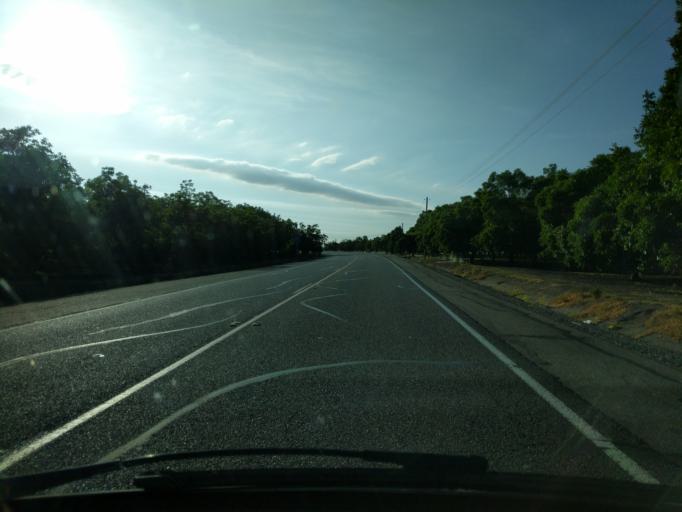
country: US
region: California
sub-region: San Joaquin County
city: Garden Acres
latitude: 37.9474
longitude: -121.1603
